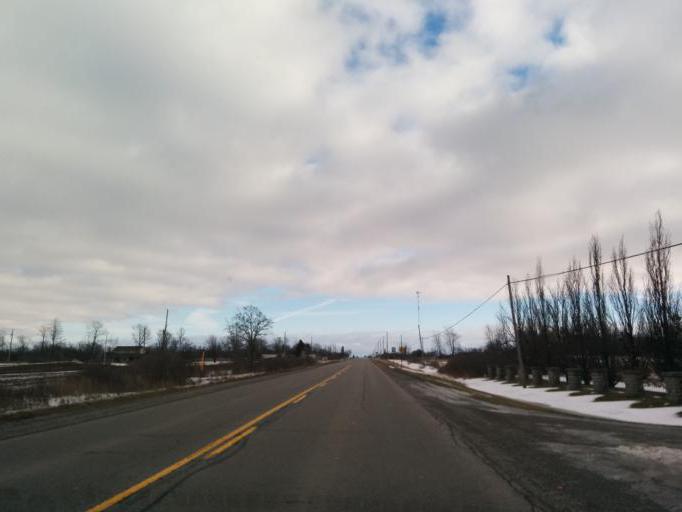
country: CA
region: Ontario
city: Brantford
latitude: 42.9736
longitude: -80.0834
